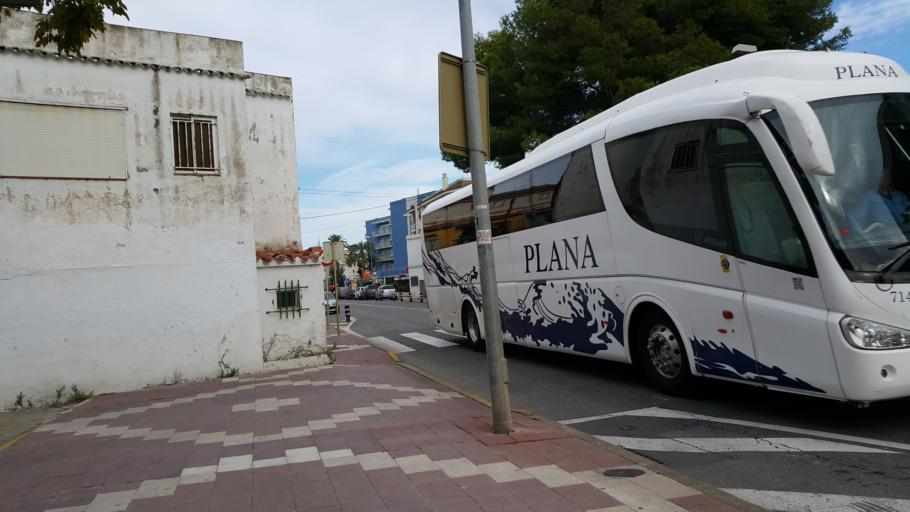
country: ES
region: Catalonia
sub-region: Provincia de Tarragona
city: Salou
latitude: 41.0738
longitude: 1.1132
